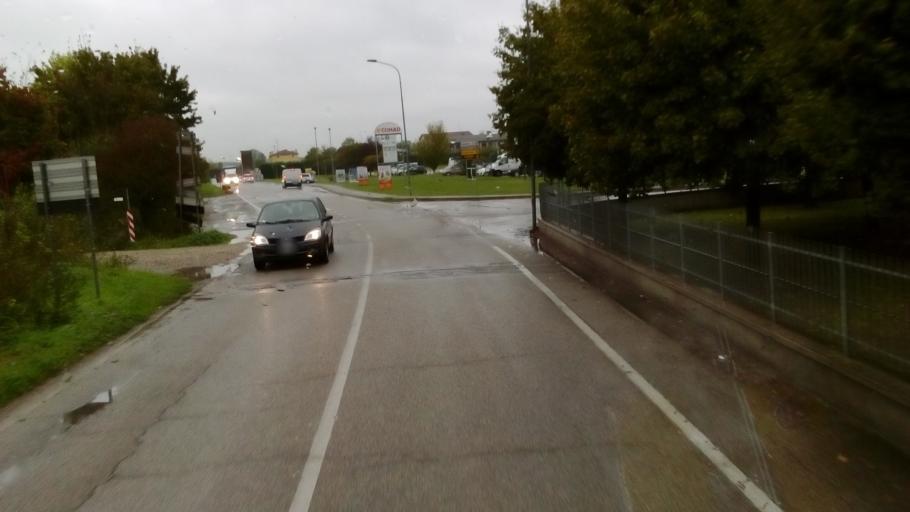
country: IT
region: Emilia-Romagna
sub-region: Provincia di Reggio Emilia
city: Luzzara
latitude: 44.9536
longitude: 10.6918
